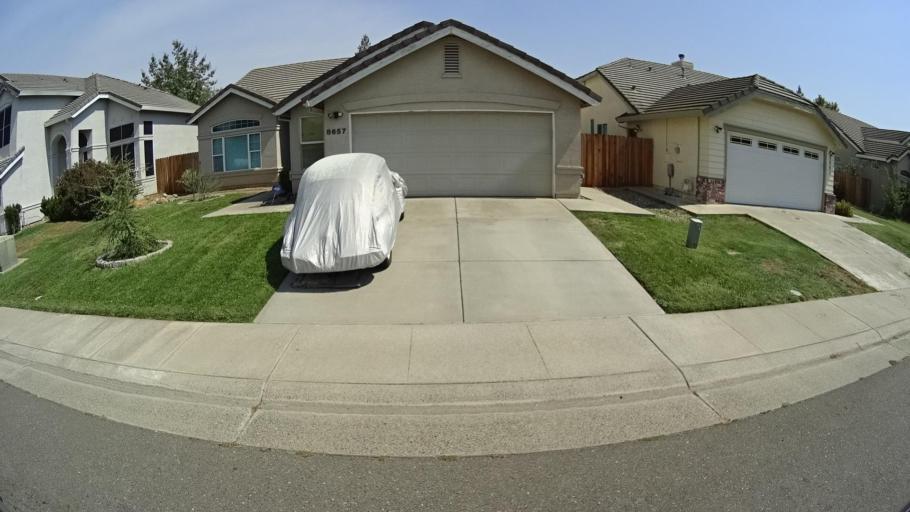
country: US
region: California
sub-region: Sacramento County
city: Elk Grove
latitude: 38.4430
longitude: -121.3751
